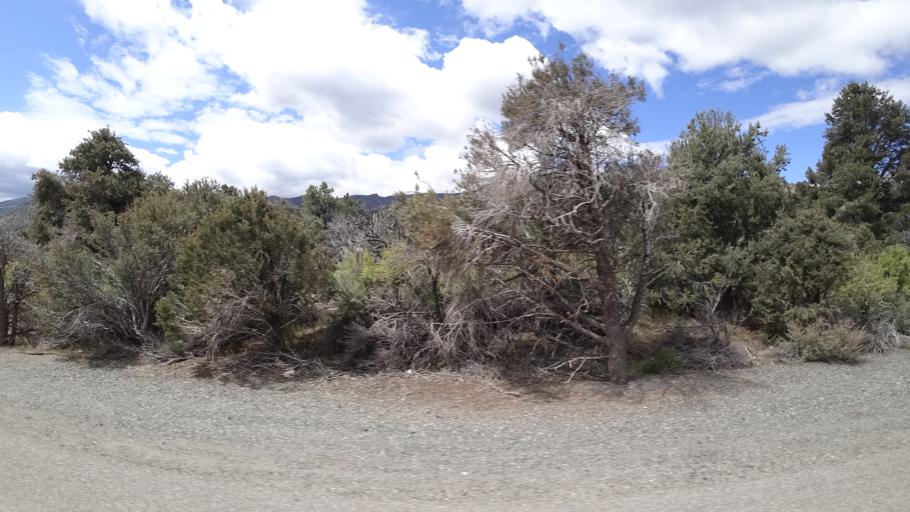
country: US
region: Nevada
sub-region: Douglas County
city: Gardnerville Ranchos
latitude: 38.7558
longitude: -119.5732
